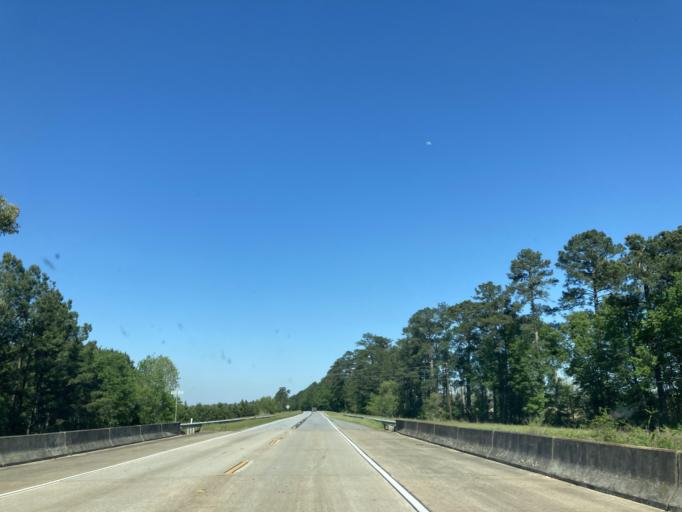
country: US
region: Georgia
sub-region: Baker County
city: Newton
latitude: 31.3303
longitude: -84.3305
